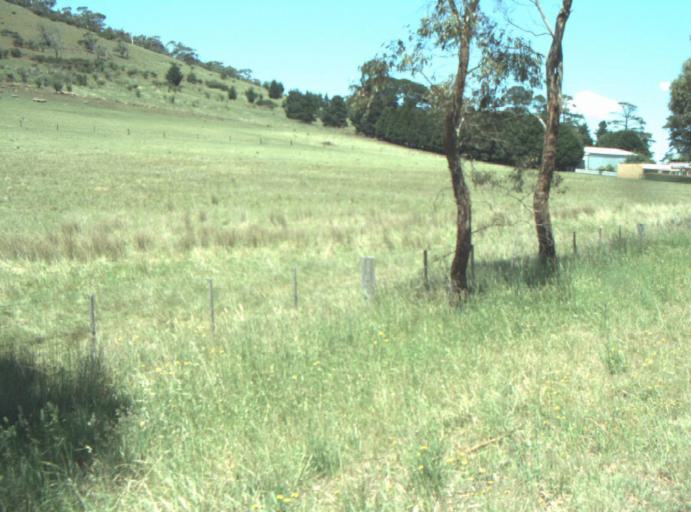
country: AU
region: Victoria
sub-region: Greater Geelong
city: Lara
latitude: -37.8807
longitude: 144.2633
